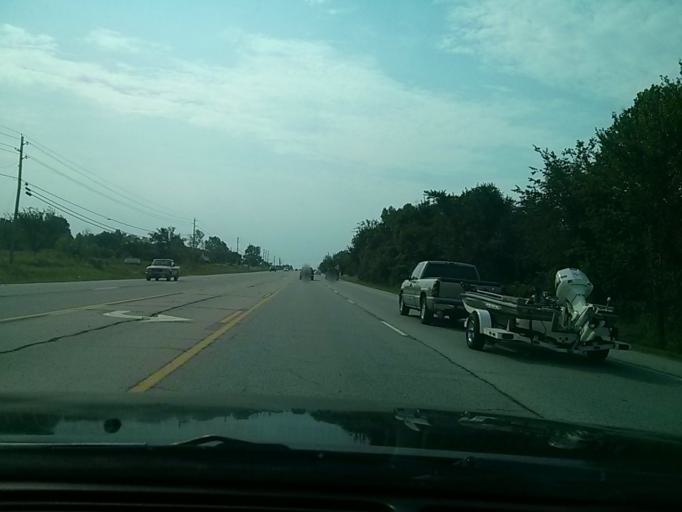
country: US
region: Oklahoma
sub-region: Wagoner County
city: Coweta
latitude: 35.9820
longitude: -95.6671
